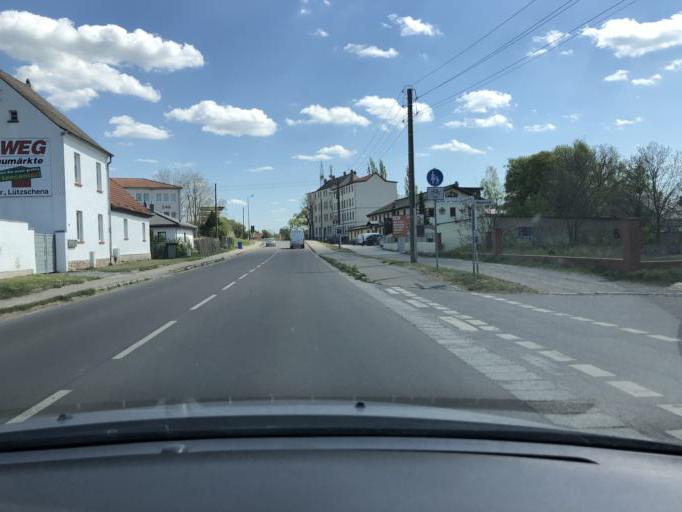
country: DE
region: Saxony
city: Schkeuditz
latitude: 51.3864
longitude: 12.2549
